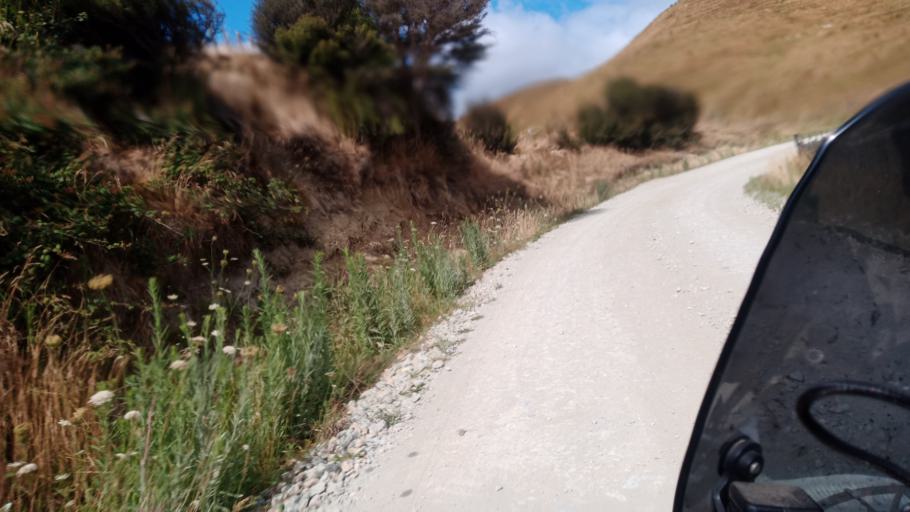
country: NZ
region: Hawke's Bay
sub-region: Wairoa District
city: Wairoa
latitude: -38.6036
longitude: 177.4774
